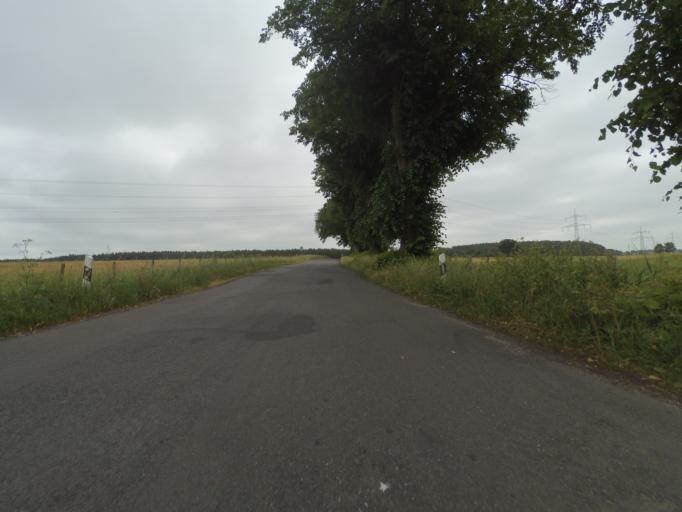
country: DE
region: Mecklenburg-Vorpommern
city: Demen
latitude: 53.6458
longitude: 11.8135
